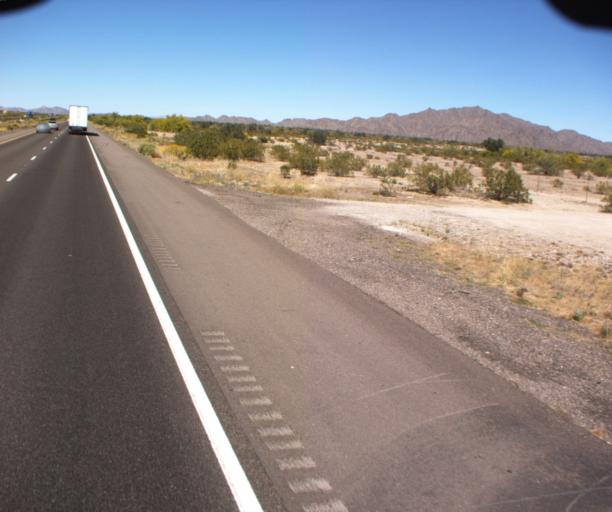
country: US
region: Arizona
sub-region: Maricopa County
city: Gila Bend
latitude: 33.1074
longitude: -112.6495
